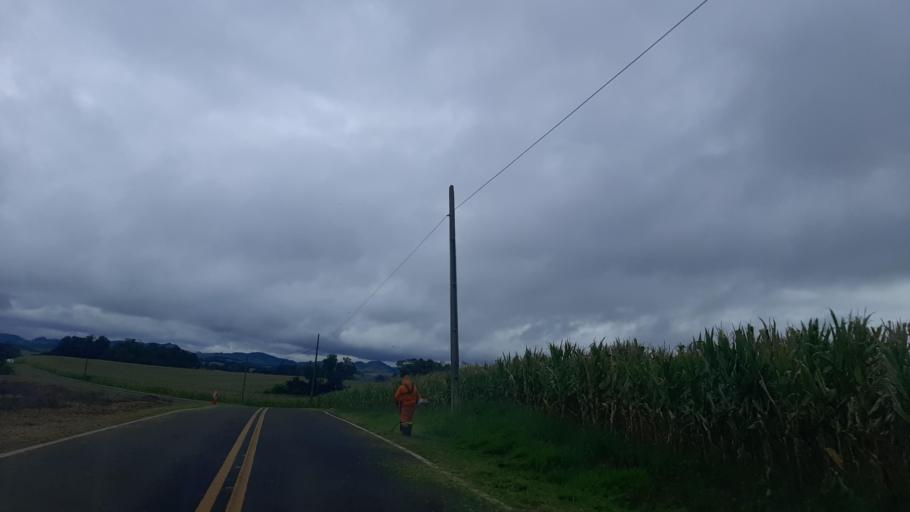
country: BR
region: Parana
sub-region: Ampere
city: Ampere
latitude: -25.9573
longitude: -53.4486
